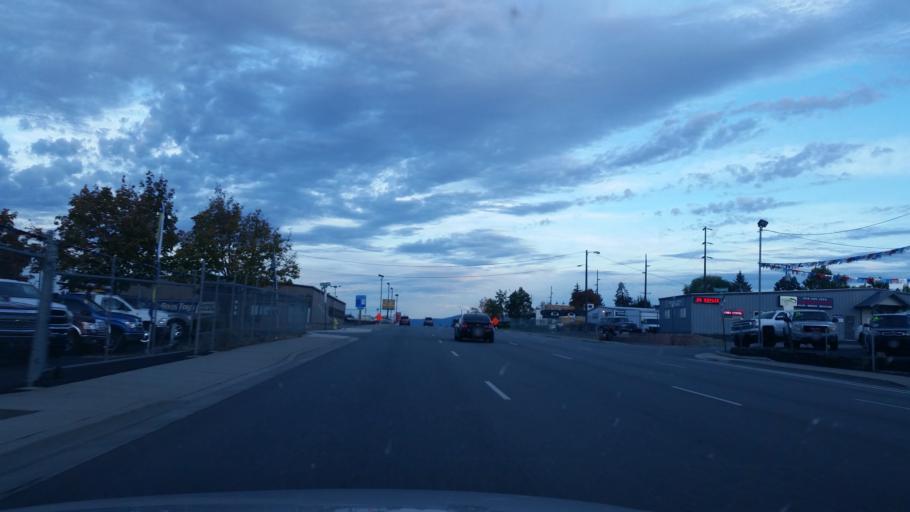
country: US
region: Washington
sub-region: Spokane County
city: Dishman
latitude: 47.6561
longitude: -117.3142
